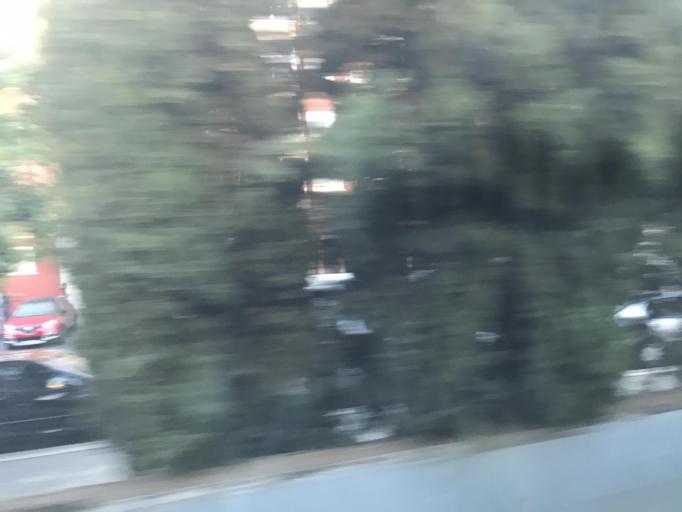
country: ES
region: Castille and Leon
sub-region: Provincia de Valladolid
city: Valladolid
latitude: 41.6475
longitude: -4.7132
